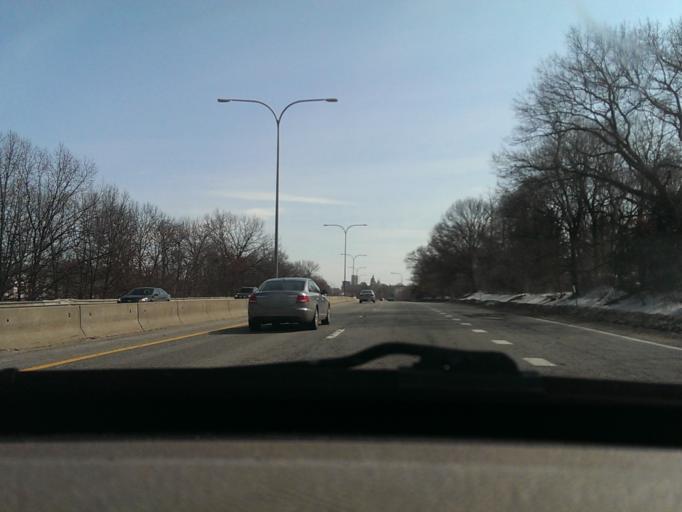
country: US
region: Rhode Island
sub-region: Providence County
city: Providence
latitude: 41.8581
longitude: -71.4291
